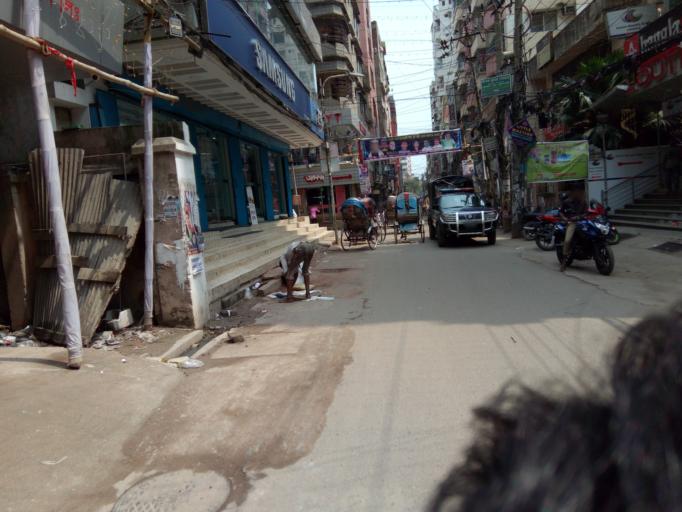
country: BD
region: Dhaka
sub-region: Dhaka
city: Dhaka
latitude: 23.7205
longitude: 90.4165
